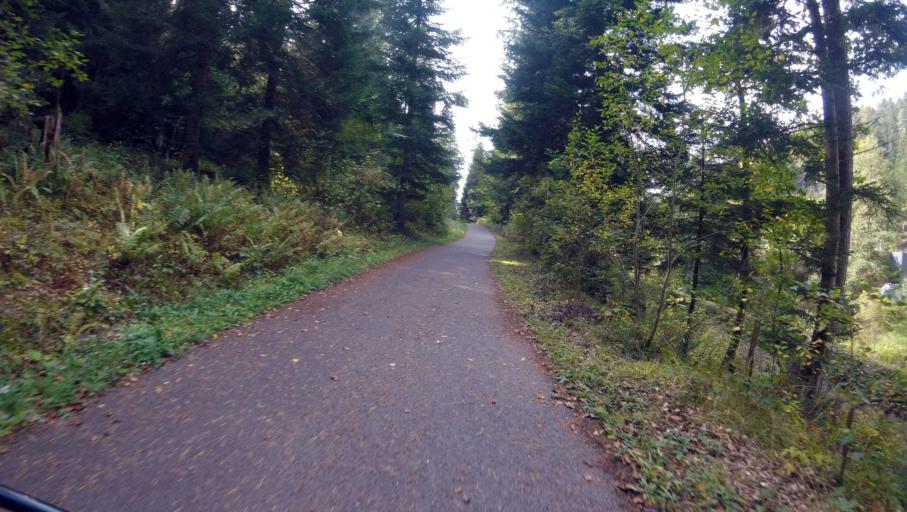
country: DE
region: Baden-Wuerttemberg
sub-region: Karlsruhe Region
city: Altensteig
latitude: 48.5878
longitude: 8.5861
